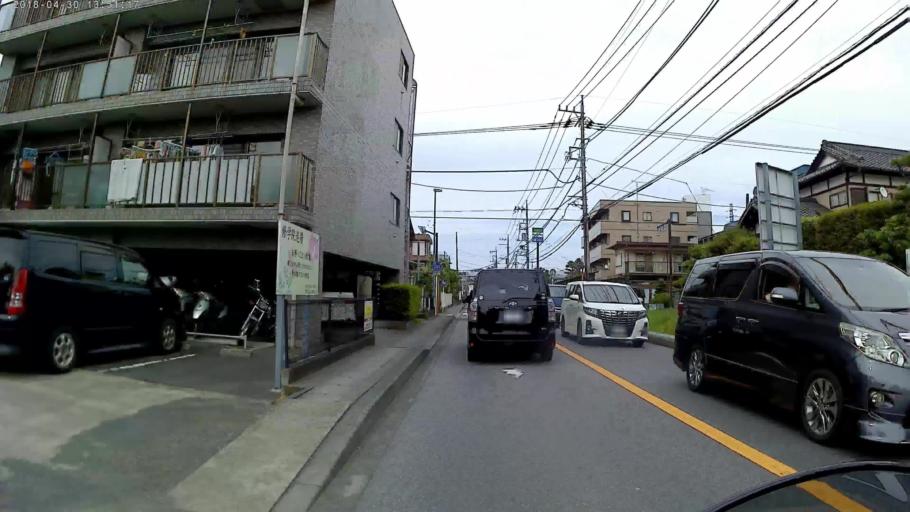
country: JP
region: Tokyo
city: Hachioji
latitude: 35.5913
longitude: 139.3727
